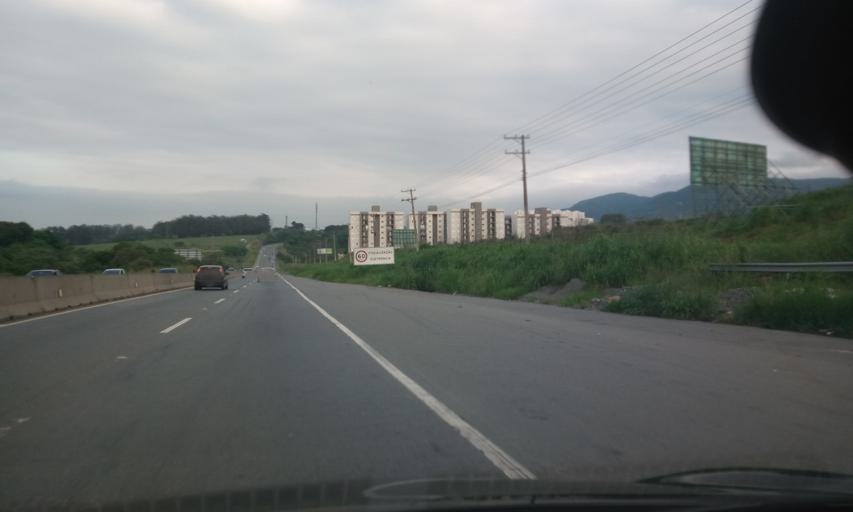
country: BR
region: Sao Paulo
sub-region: Itupeva
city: Itupeva
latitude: -23.1767
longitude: -46.9817
